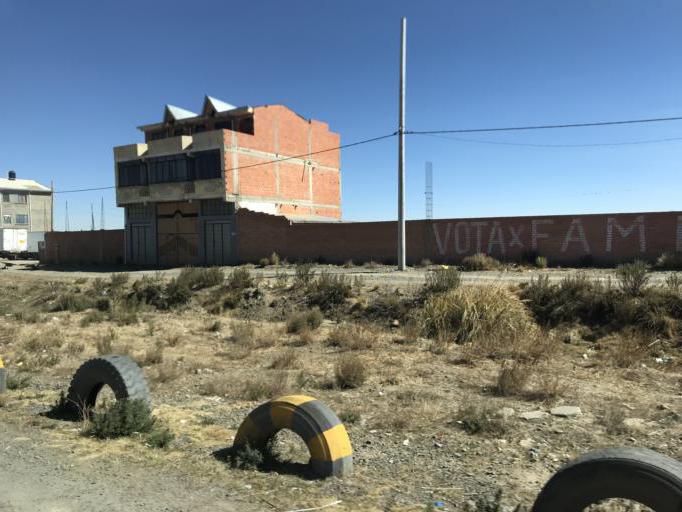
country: BO
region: La Paz
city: La Paz
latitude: -16.5144
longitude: -68.2793
